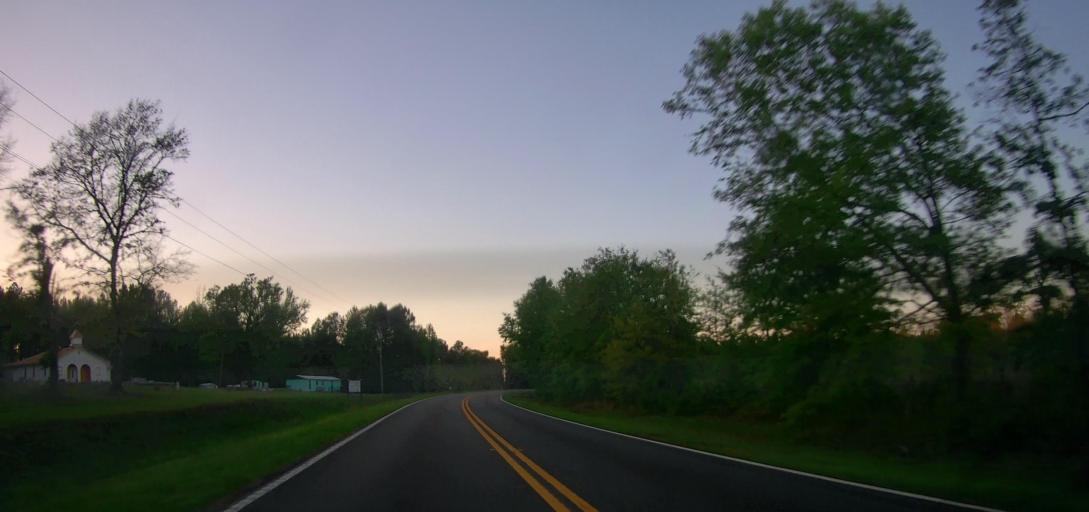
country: US
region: Georgia
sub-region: Marion County
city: Buena Vista
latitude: 32.3757
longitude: -84.5577
